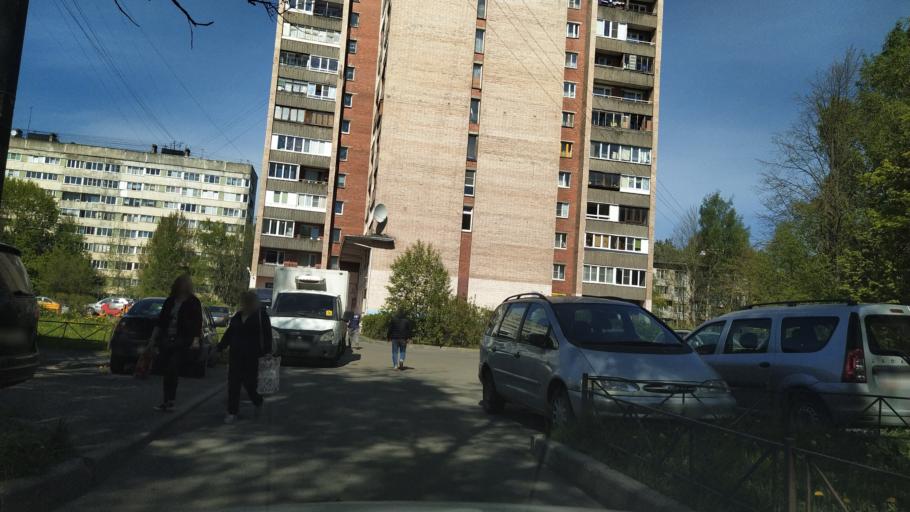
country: RU
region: St.-Petersburg
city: Grazhdanka
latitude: 60.0407
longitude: 30.4206
